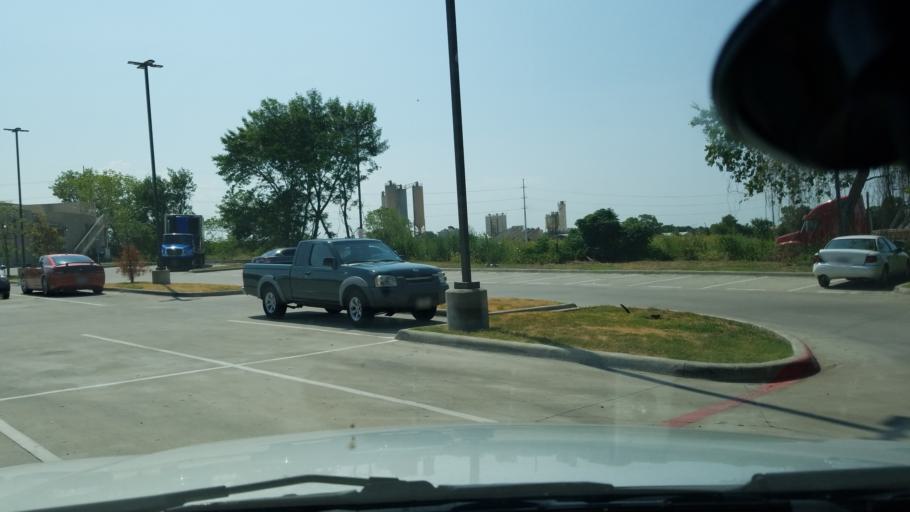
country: US
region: Texas
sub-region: Dallas County
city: Farmers Branch
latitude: 32.8653
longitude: -96.9092
